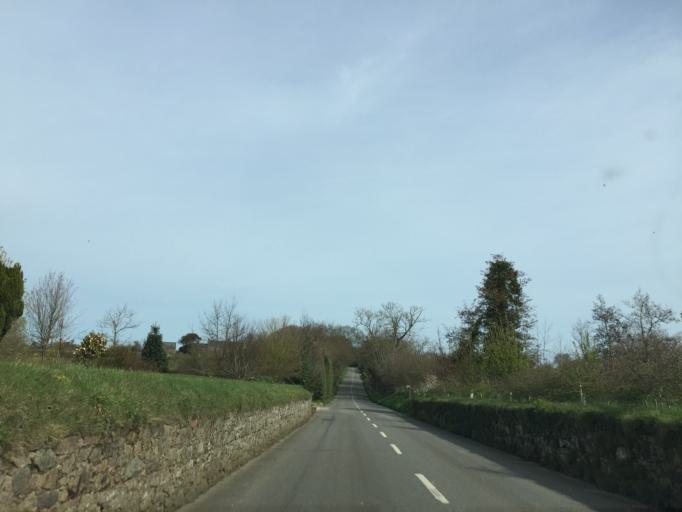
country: JE
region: St Helier
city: Saint Helier
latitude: 49.2240
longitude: -2.0585
